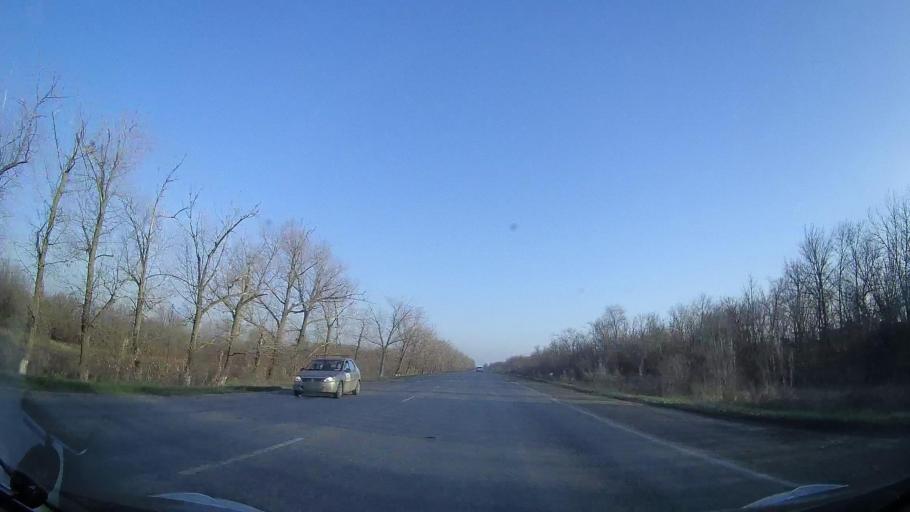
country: RU
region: Rostov
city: Bataysk
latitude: 47.0718
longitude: 39.7933
